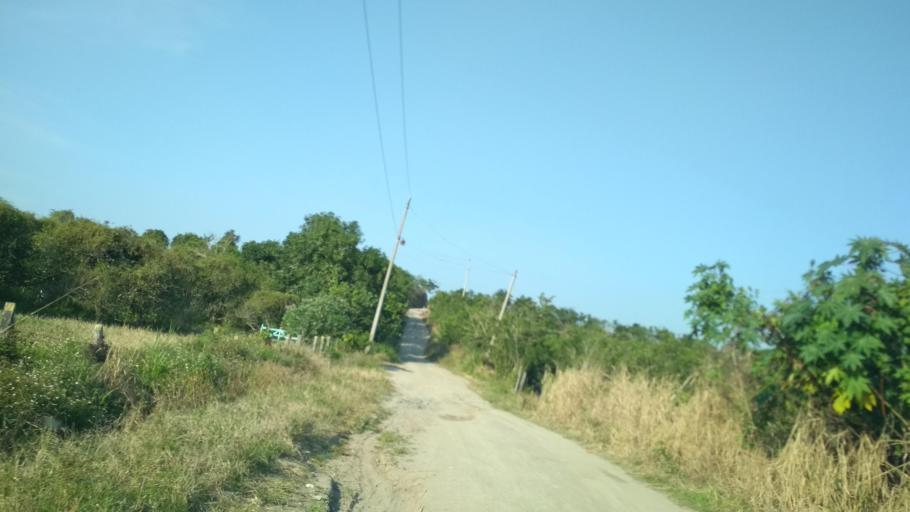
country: MX
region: Puebla
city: San Jose Acateno
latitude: 20.2211
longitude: -97.2621
